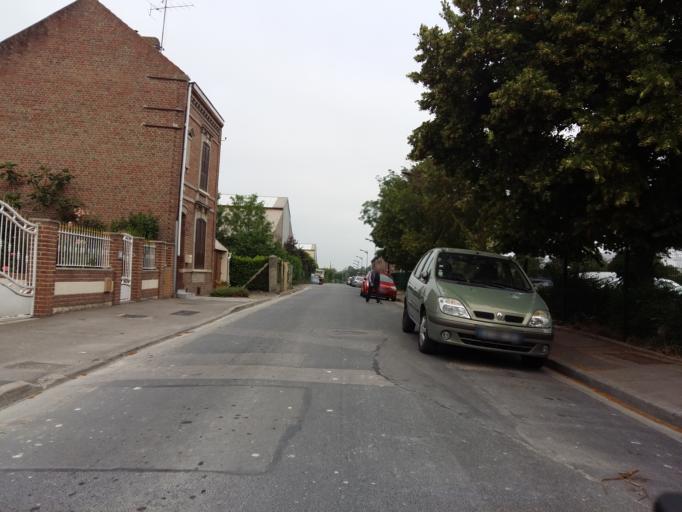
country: FR
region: Picardie
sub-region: Departement de la Somme
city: Amiens
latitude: 49.9090
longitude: 2.2907
